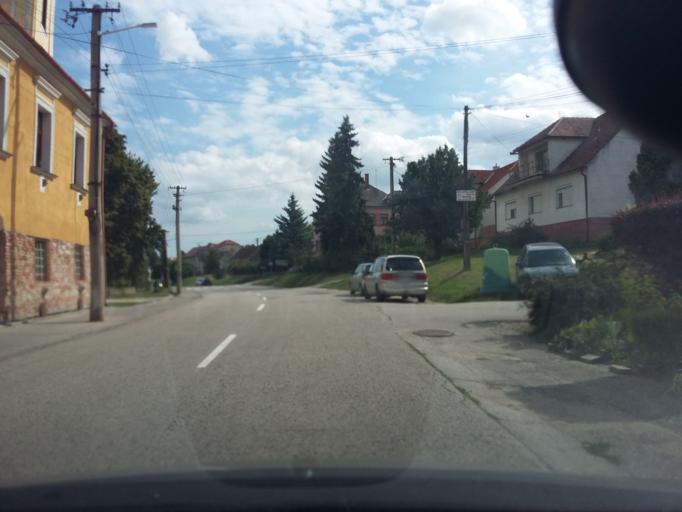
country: SK
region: Trnavsky
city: Gbely
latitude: 48.7214
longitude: 17.1606
